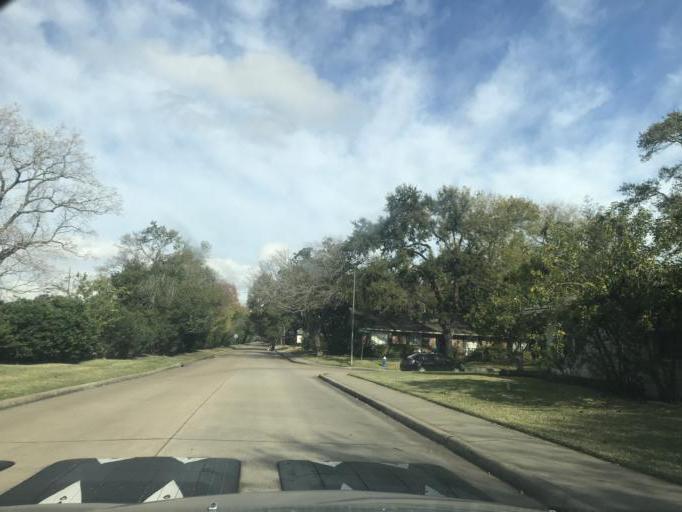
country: US
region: Texas
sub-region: Harris County
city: Hunters Creek Village
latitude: 29.7445
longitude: -95.4954
